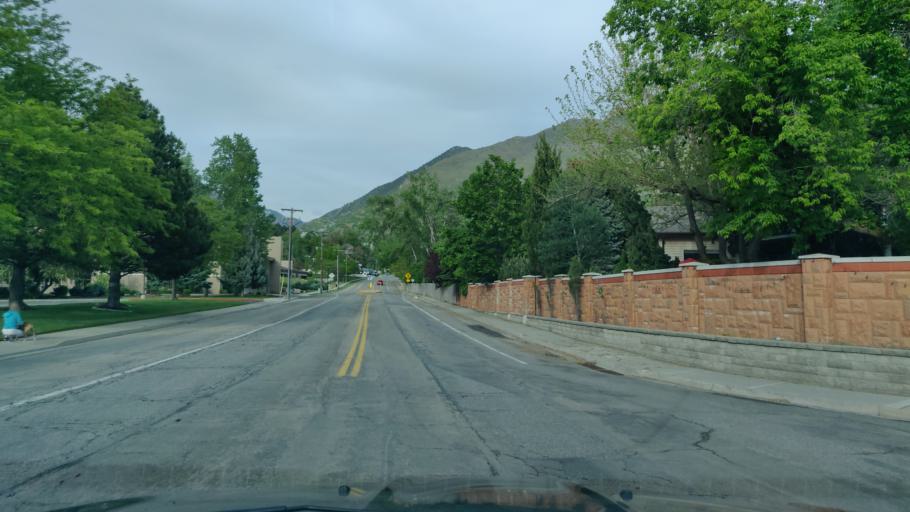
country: US
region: Utah
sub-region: Salt Lake County
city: Cottonwood Heights
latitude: 40.6037
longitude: -111.8100
